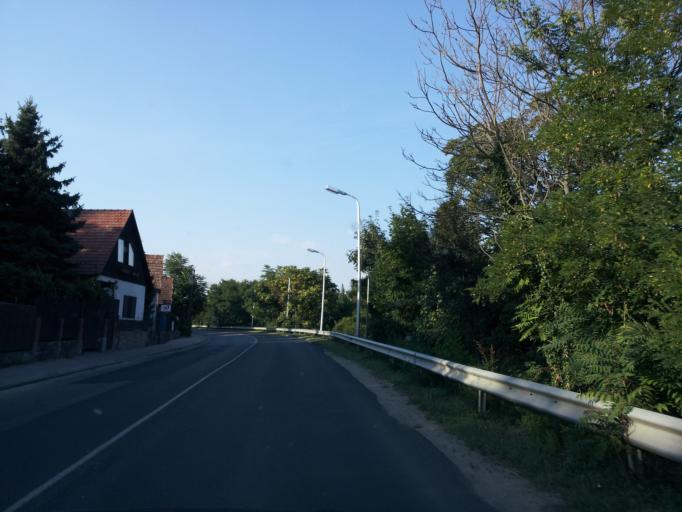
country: HU
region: Pest
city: Leanyfalu
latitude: 47.7236
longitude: 19.0891
